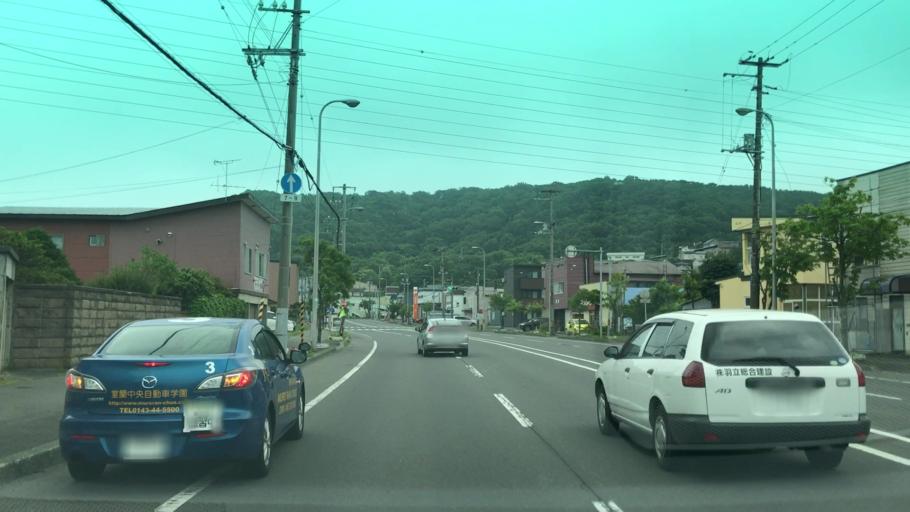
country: JP
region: Hokkaido
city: Muroran
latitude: 42.3570
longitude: 141.0459
